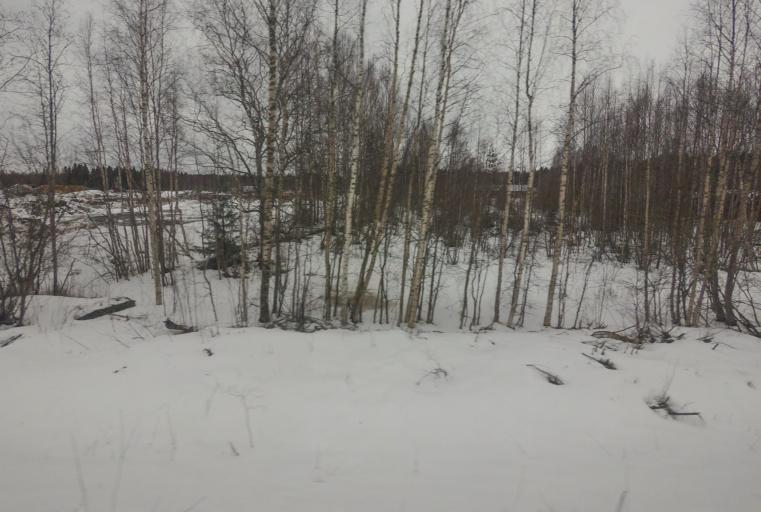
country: FI
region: Southern Savonia
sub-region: Savonlinna
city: Savonlinna
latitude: 61.8567
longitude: 28.9715
